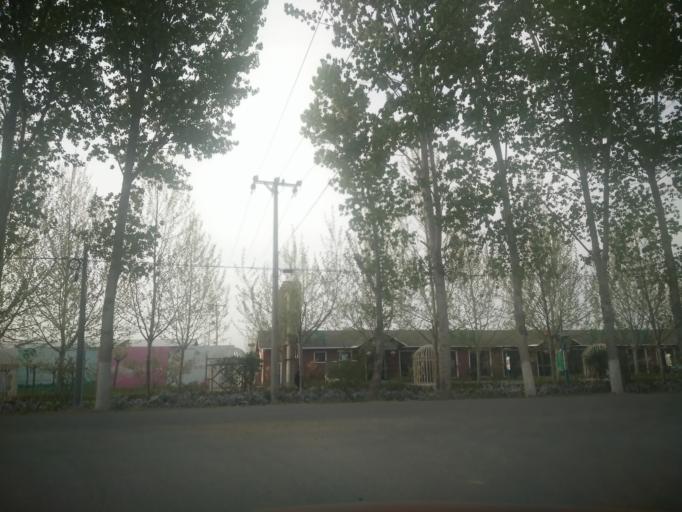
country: CN
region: Beijing
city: Weishanzhuang
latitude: 39.6757
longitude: 116.4444
